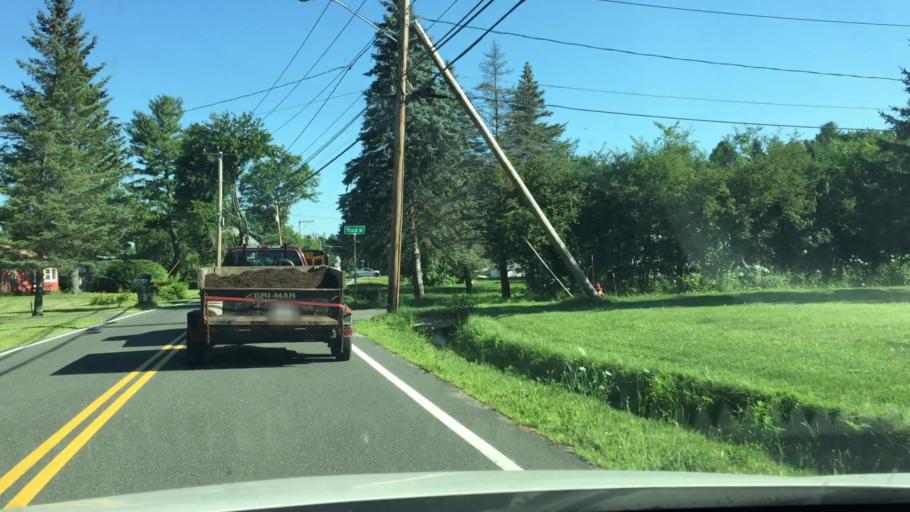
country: US
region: Massachusetts
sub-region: Berkshire County
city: Lee
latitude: 42.2913
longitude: -73.2382
